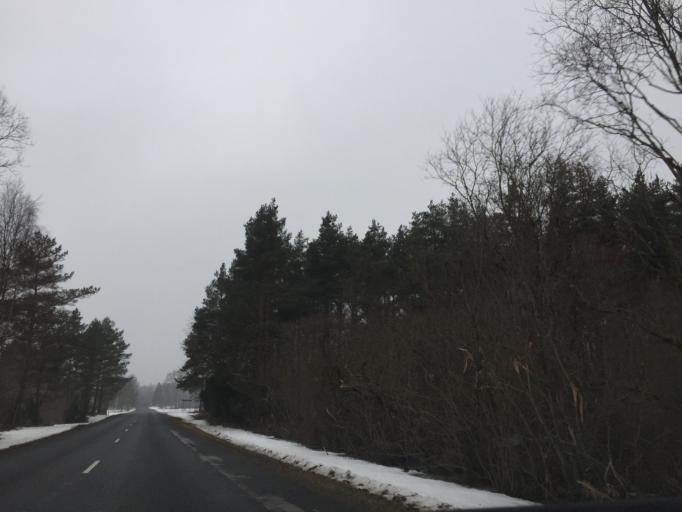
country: EE
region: Saare
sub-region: Orissaare vald
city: Orissaare
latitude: 58.4042
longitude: 22.7985
